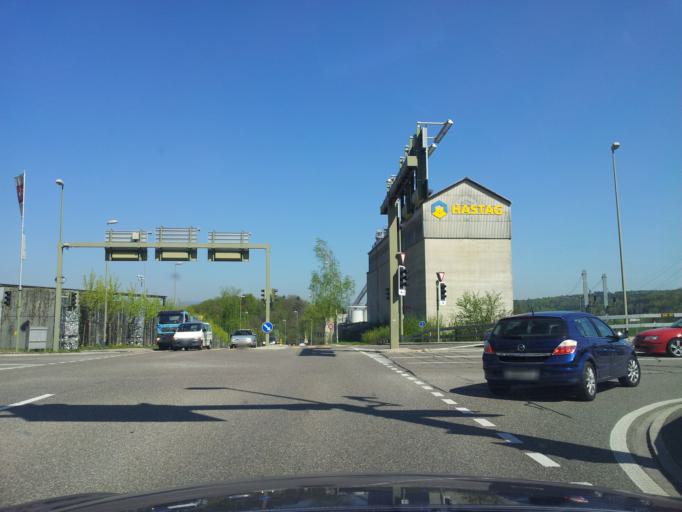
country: CH
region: Zurich
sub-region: Bezirk Dietikon
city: Birmensdorf
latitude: 47.3632
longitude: 8.4312
